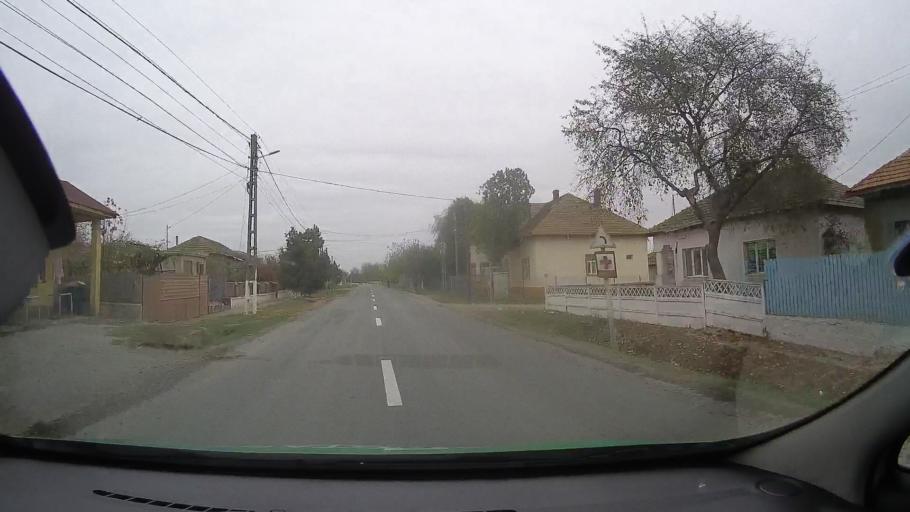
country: RO
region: Constanta
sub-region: Comuna Silistea
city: Silistea
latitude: 44.4447
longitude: 28.2367
